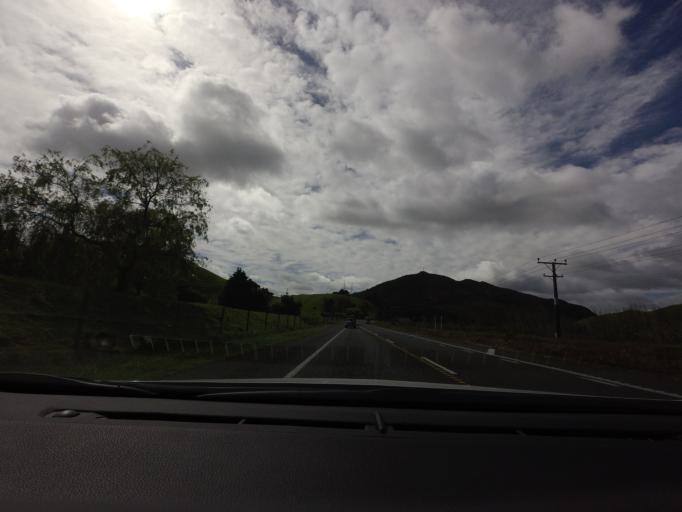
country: NZ
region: Bay of Plenty
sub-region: Rotorua District
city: Rotorua
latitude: -38.3069
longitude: 176.3728
